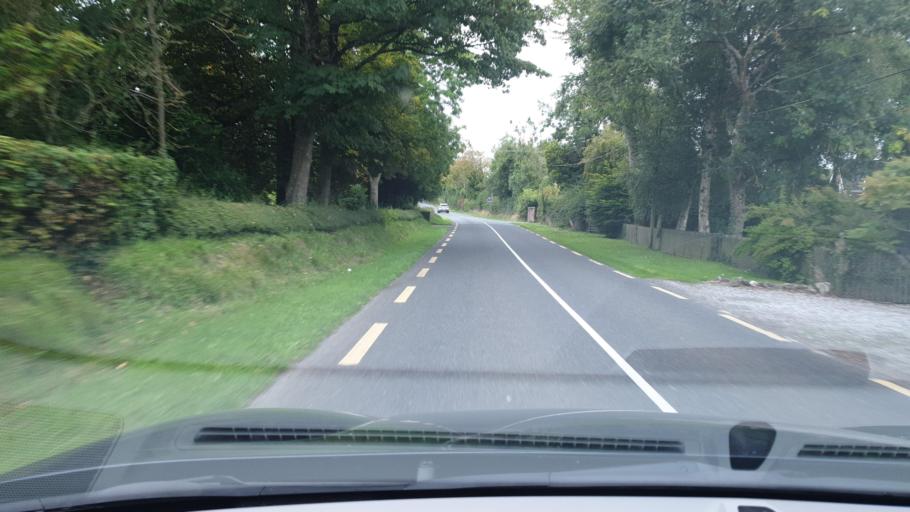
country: IE
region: Leinster
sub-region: An Mhi
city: Dunshaughlin
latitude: 53.5500
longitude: -6.5213
